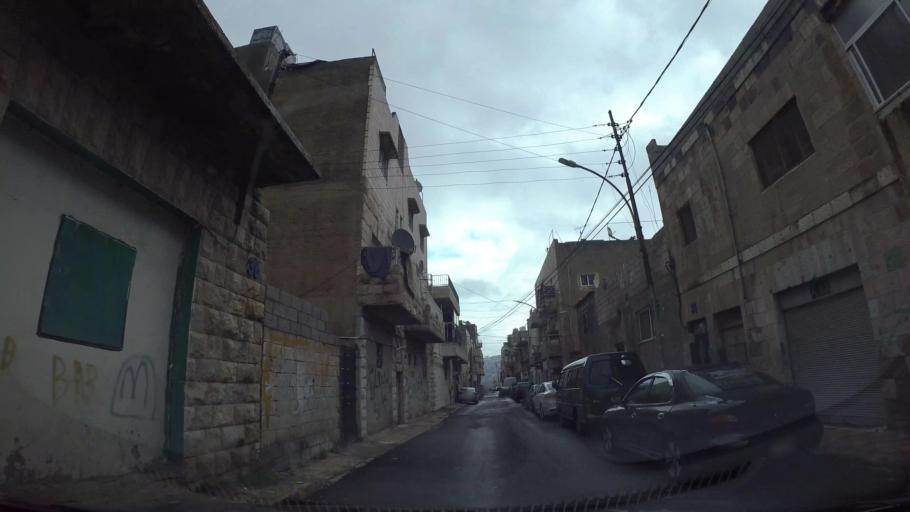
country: JO
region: Amman
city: Amman
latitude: 31.9474
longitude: 35.9200
